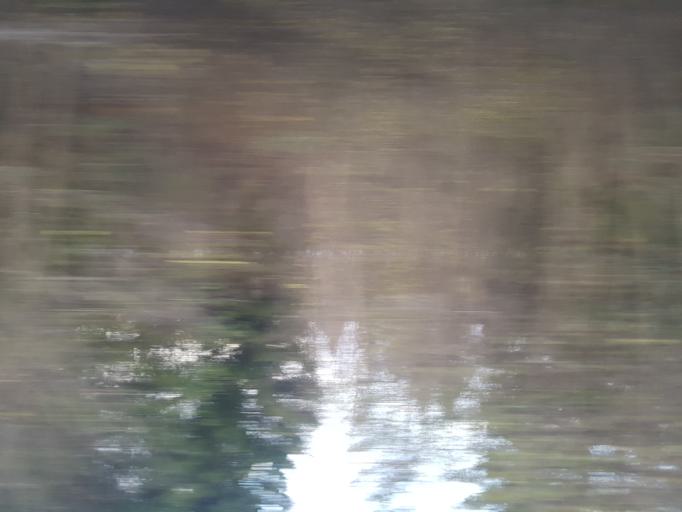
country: NO
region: Sor-Trondelag
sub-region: Melhus
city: Melhus
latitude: 63.2753
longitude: 10.2871
